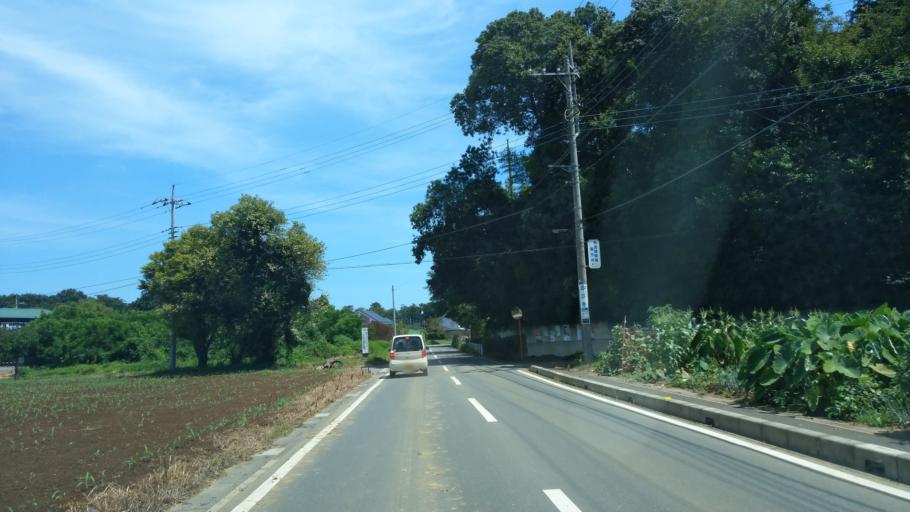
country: JP
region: Saitama
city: Ageoshimo
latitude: 35.9317
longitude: 139.5651
